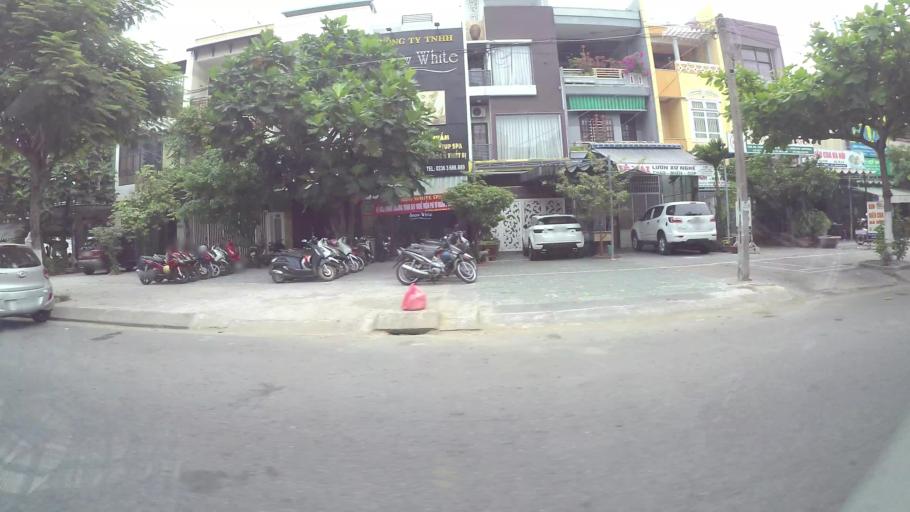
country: VN
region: Da Nang
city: Cam Le
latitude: 16.0391
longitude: 108.2179
